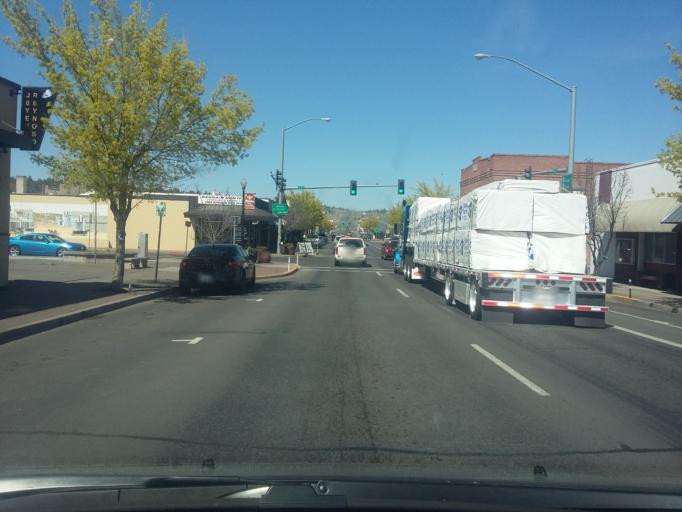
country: US
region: Oregon
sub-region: Jefferson County
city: Madras
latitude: 44.6331
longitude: -121.1296
